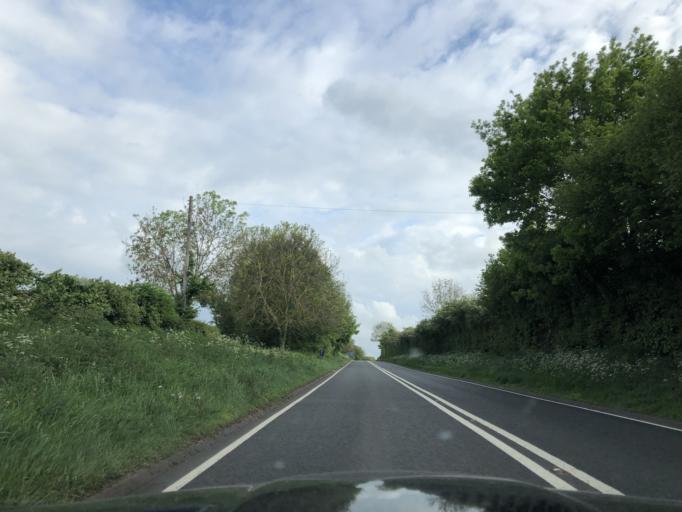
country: GB
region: England
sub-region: Gloucestershire
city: Moreton in Marsh
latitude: 52.0156
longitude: -1.6902
